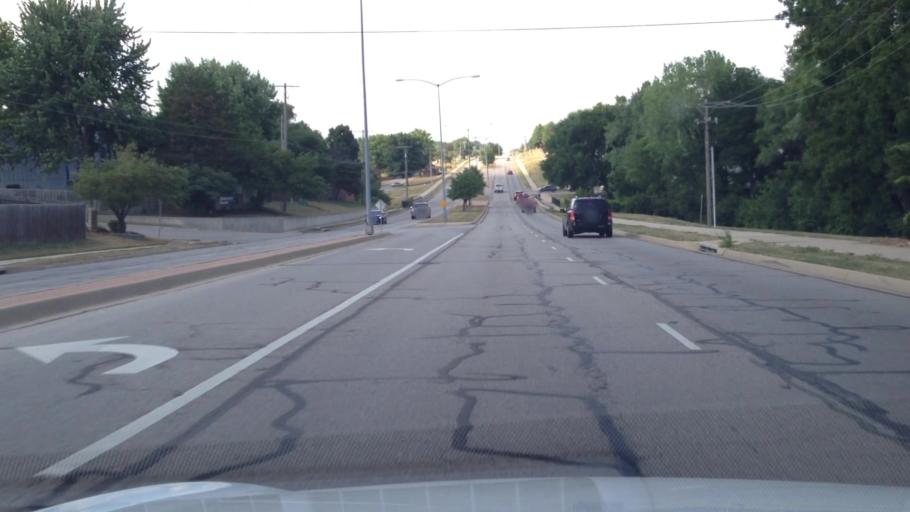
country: US
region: Kansas
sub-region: Johnson County
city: Olathe
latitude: 38.9052
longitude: -94.7973
